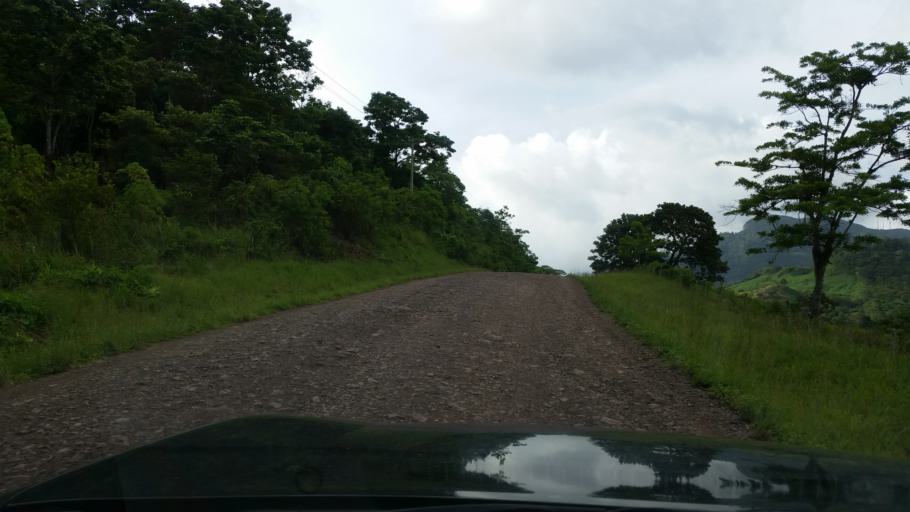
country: NI
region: Jinotega
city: Jinotega
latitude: 13.2256
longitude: -85.7302
